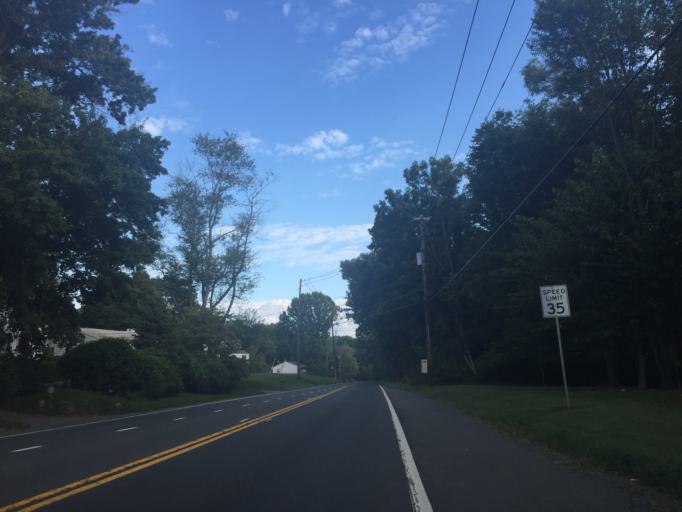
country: US
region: Maryland
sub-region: Montgomery County
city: Montgomery Village
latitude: 39.2079
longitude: -77.1691
